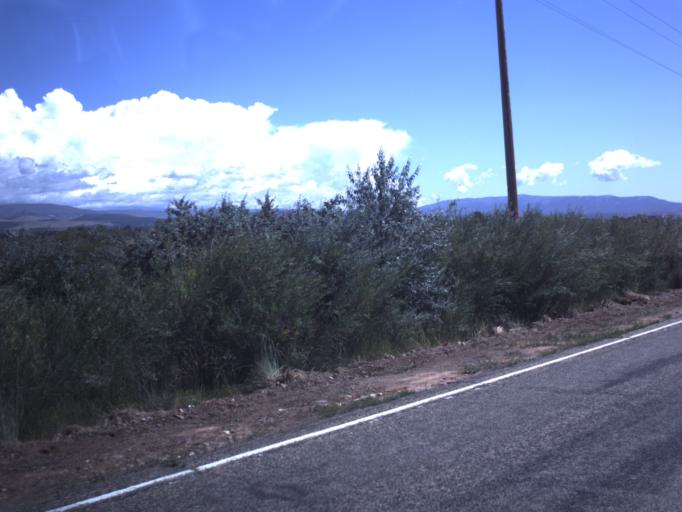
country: US
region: Utah
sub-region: Duchesne County
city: Roosevelt
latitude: 40.4329
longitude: -109.9475
